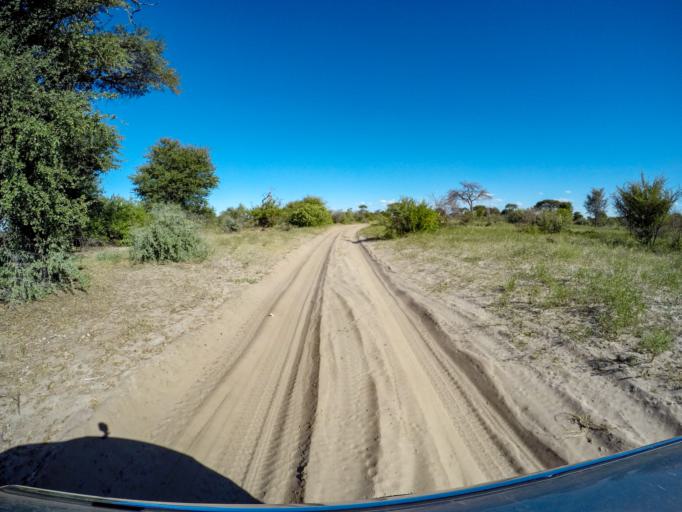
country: BW
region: Central
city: Rakops
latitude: -20.4482
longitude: 24.5167
